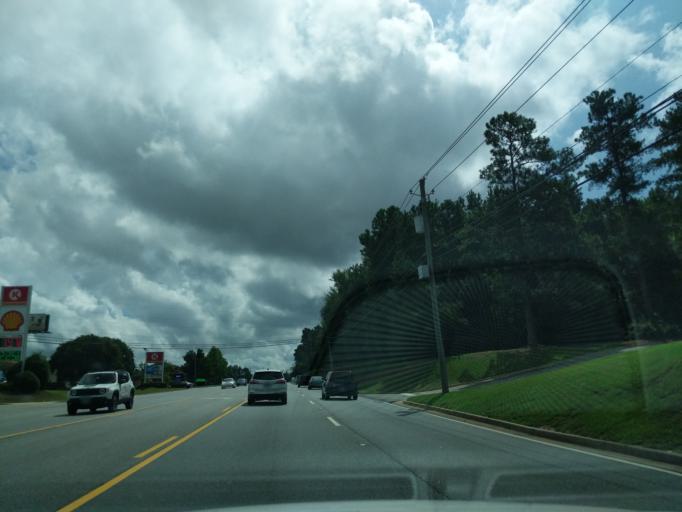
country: US
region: Georgia
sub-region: Columbia County
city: Evans
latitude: 33.5433
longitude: -82.1393
